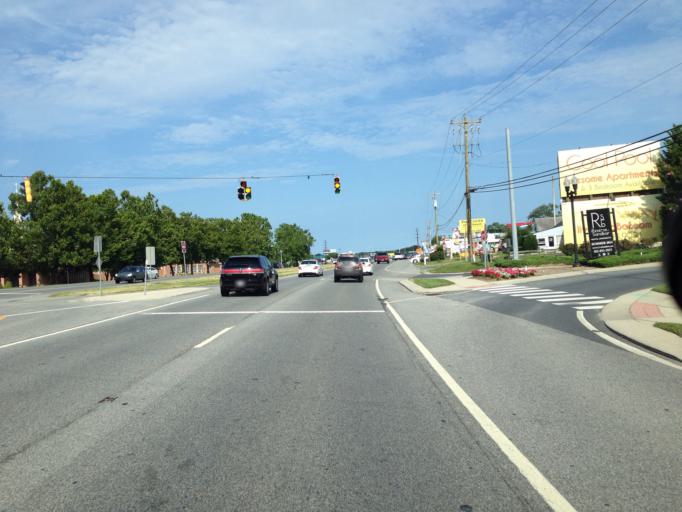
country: US
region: Delaware
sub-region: Sussex County
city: Lewes
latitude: 38.7496
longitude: -75.1824
